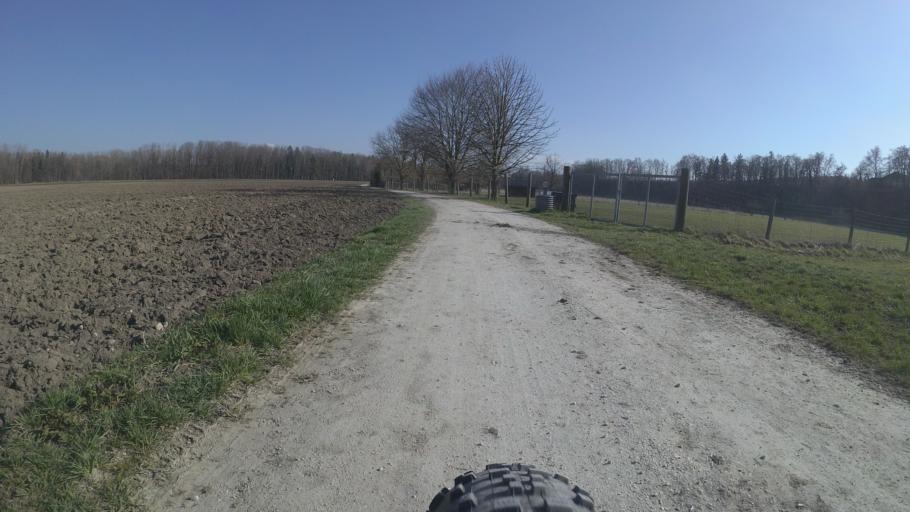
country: DE
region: Bavaria
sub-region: Upper Bavaria
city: Nussdorf
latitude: 47.9308
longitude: 12.6069
